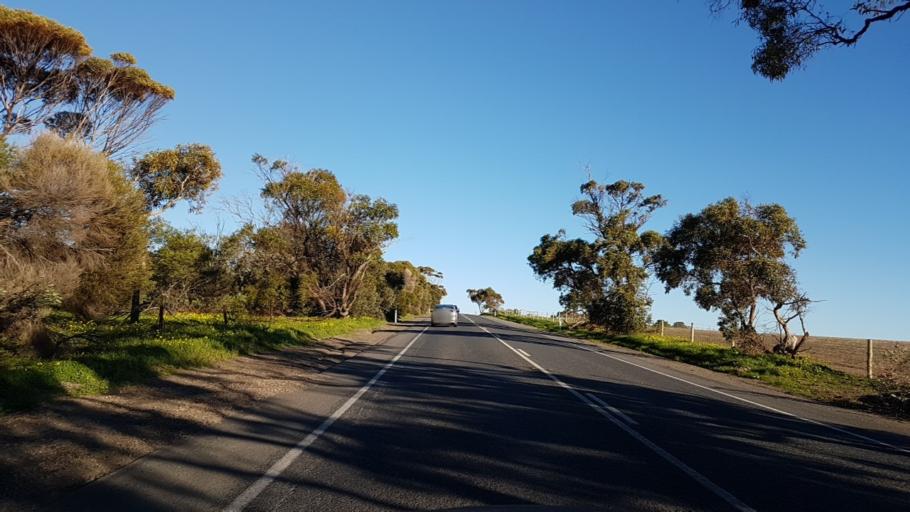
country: AU
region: South Australia
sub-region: Onkaparinga
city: Aldinga
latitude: -35.2466
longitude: 138.4944
